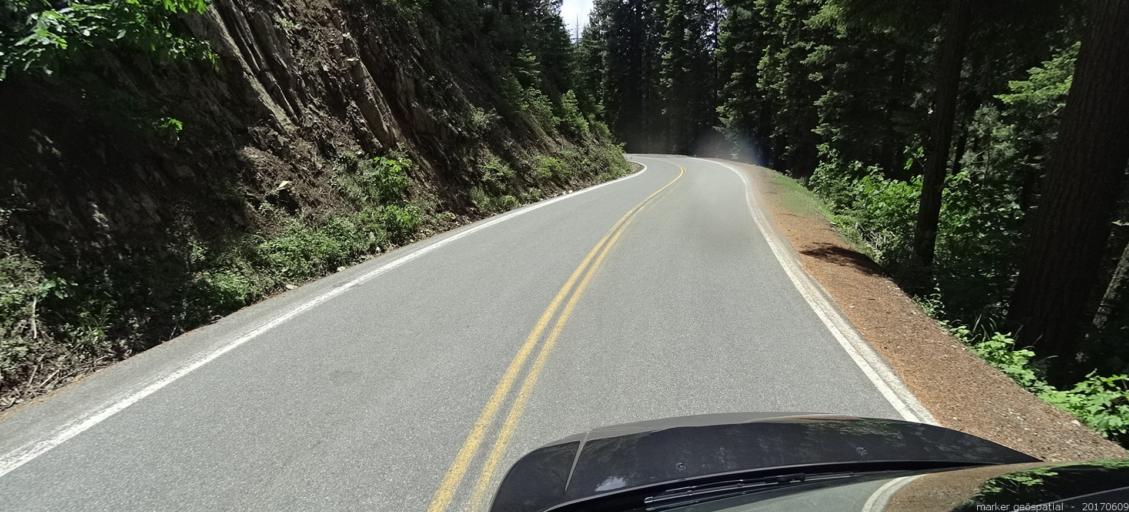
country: US
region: California
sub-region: Siskiyou County
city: Yreka
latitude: 41.3775
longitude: -123.0070
